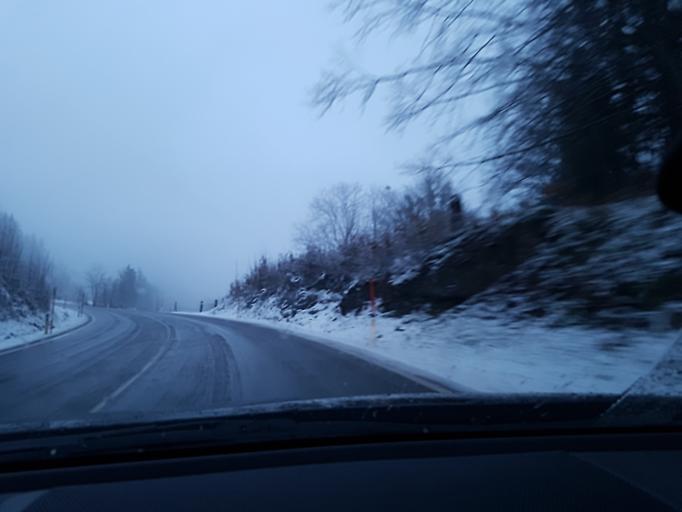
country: AT
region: Upper Austria
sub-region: Politischer Bezirk Gmunden
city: Bad Goisern
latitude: 47.6172
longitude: 13.6542
